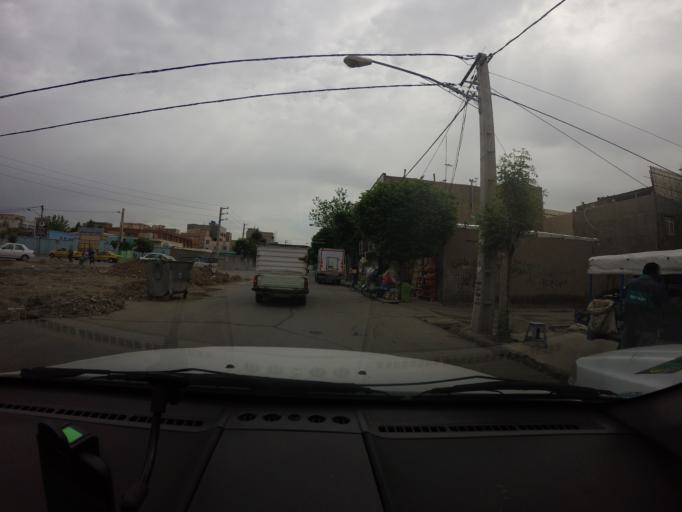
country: IR
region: Tehran
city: Eslamshahr
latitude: 35.5412
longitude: 51.2307
